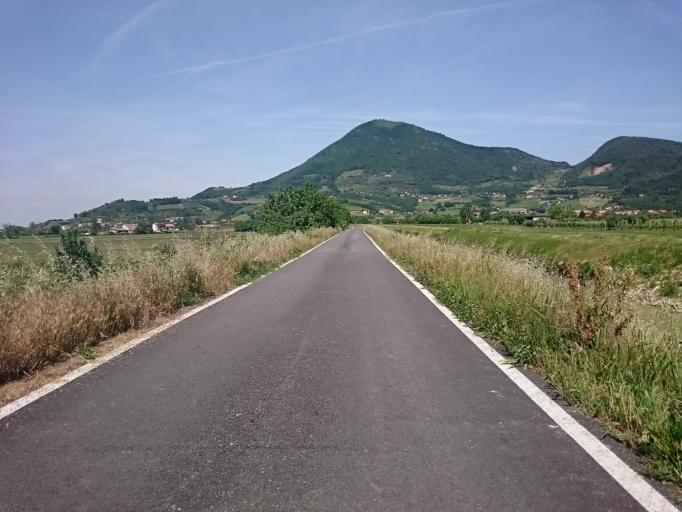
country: IT
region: Veneto
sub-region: Provincia di Padova
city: Vo
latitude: 45.3457
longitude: 11.6268
